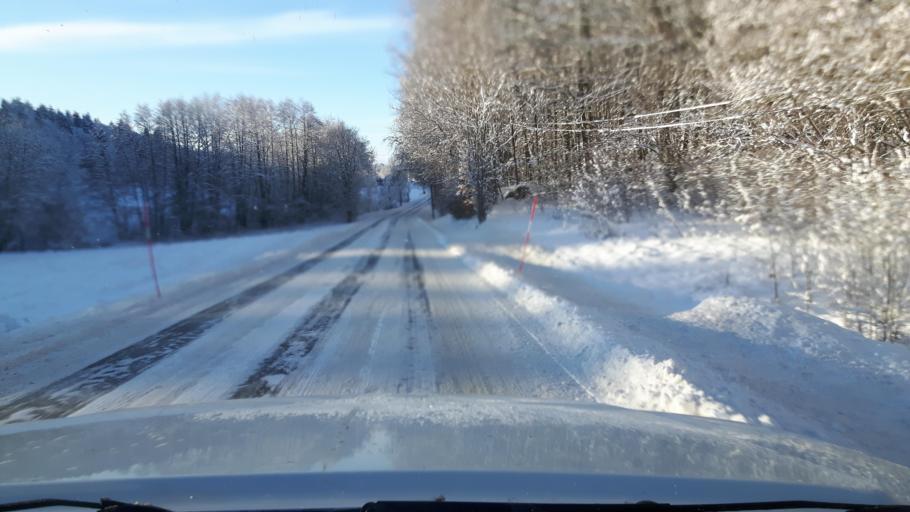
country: SE
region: Vaestra Goetaland
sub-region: Harryda Kommun
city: Landvetter
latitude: 57.5741
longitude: 12.2343
